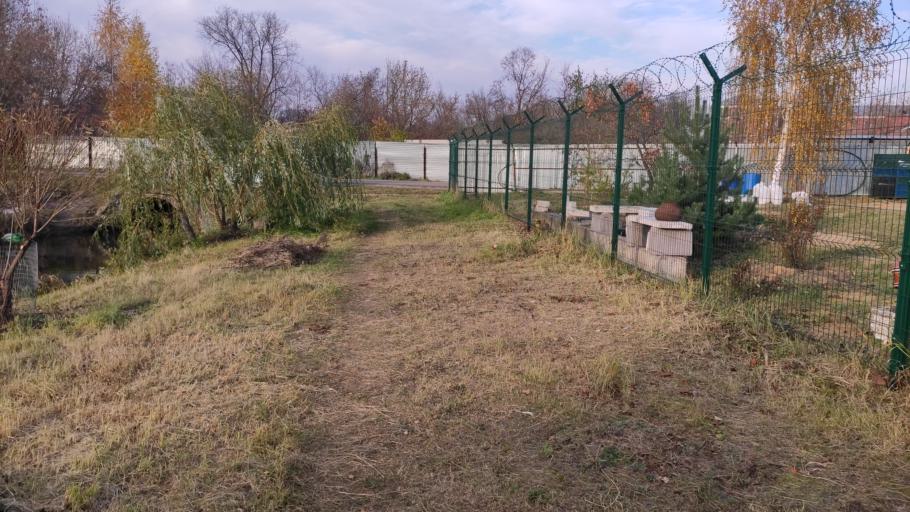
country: RU
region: Moskovskaya
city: Noginsk
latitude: 55.8750
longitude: 38.4580
